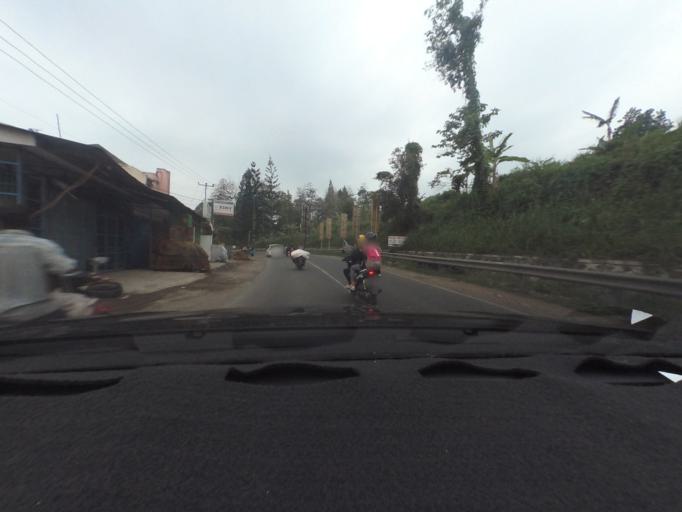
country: ID
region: West Java
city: Cicurug
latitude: -6.8038
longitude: 106.7734
